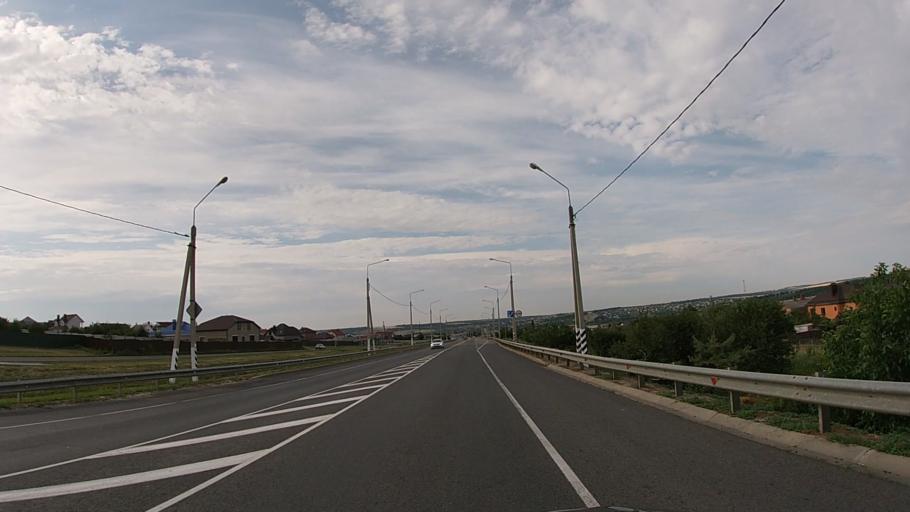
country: RU
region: Belgorod
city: Severnyy
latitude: 50.6485
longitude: 36.4681
